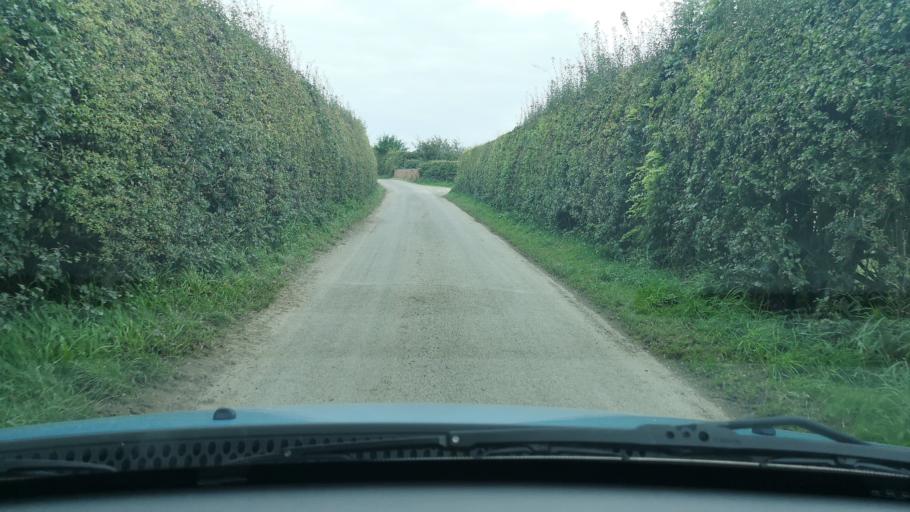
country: GB
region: England
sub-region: City and Borough of Wakefield
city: Featherstone
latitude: 53.6596
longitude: -1.3658
